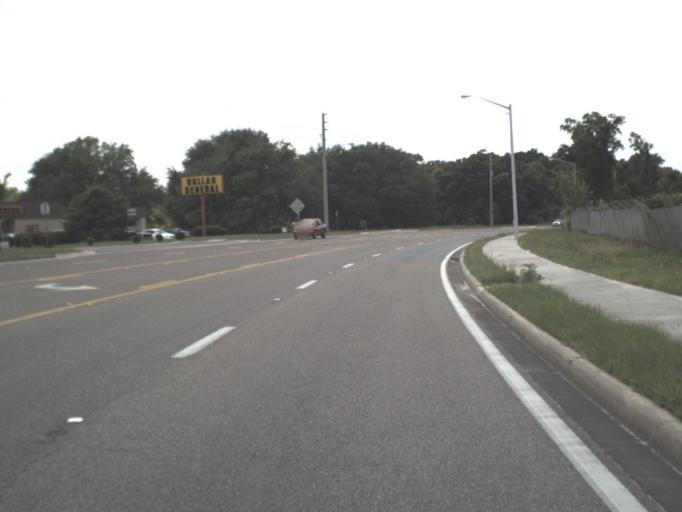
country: US
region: Florida
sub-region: Columbia County
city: Watertown
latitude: 30.1830
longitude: -82.6019
